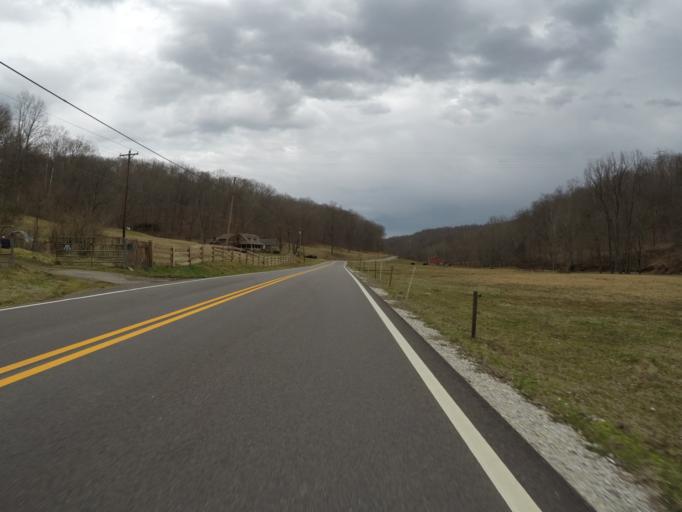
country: US
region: Ohio
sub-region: Lawrence County
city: Burlington
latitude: 38.4552
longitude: -82.5221
